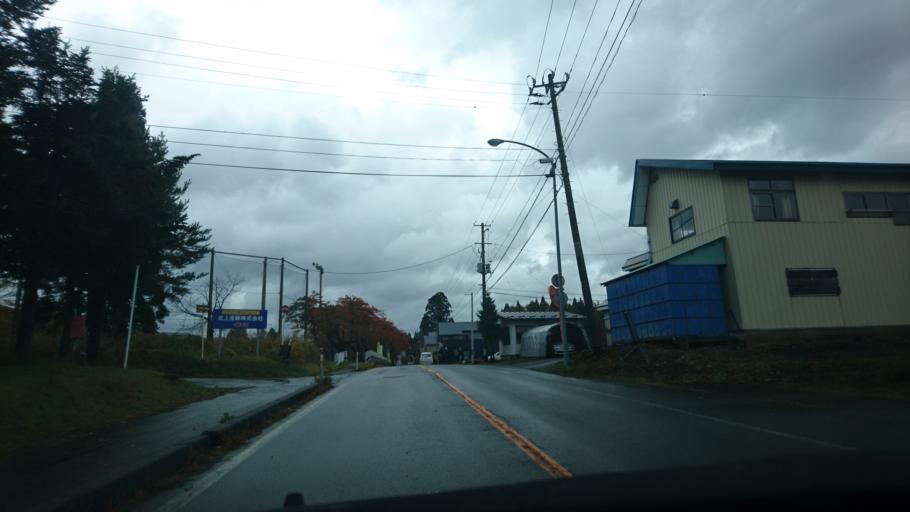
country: JP
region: Akita
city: Kakunodatemachi
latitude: 39.4525
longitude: 140.7663
